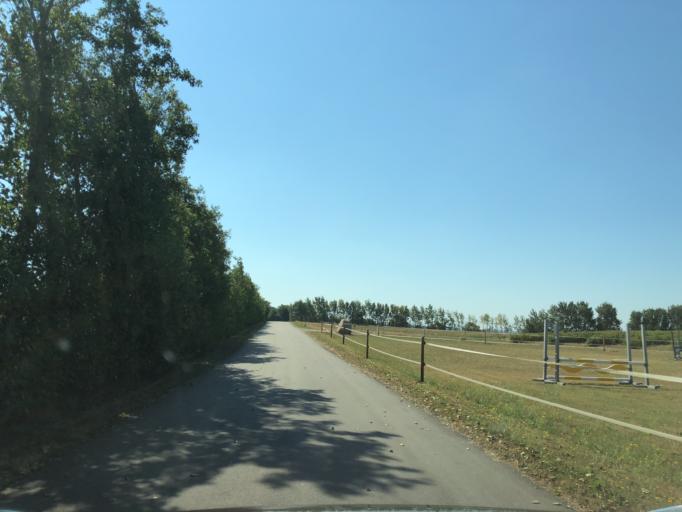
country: DK
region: Zealand
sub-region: Odsherred Kommune
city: Hojby
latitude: 55.9538
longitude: 11.4889
